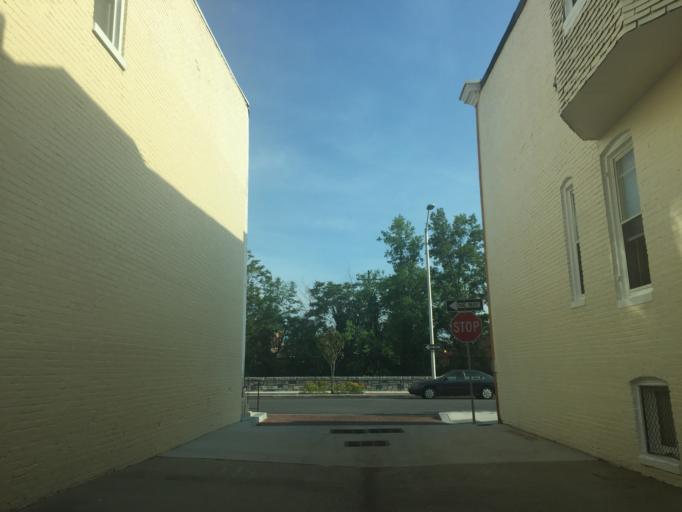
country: US
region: Maryland
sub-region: City of Baltimore
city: Baltimore
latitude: 39.3196
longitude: -76.6163
